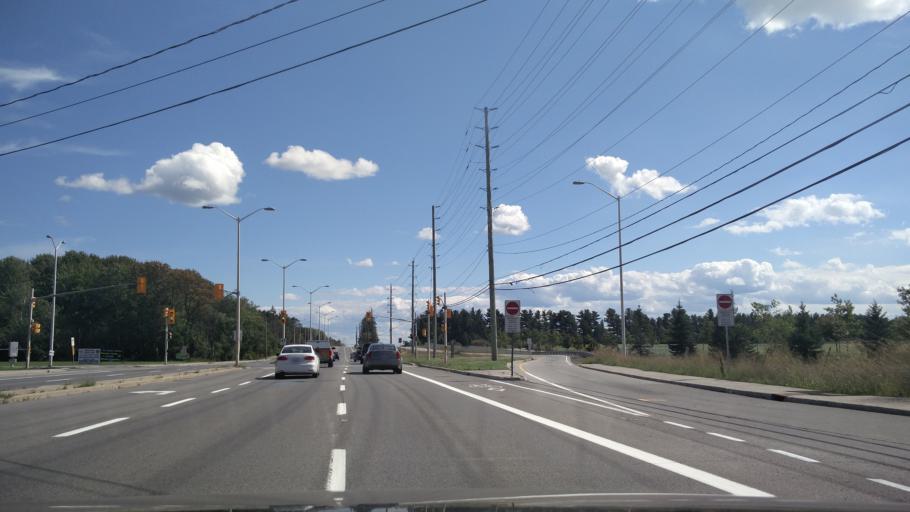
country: CA
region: Ontario
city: Bells Corners
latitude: 45.3262
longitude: -75.7474
